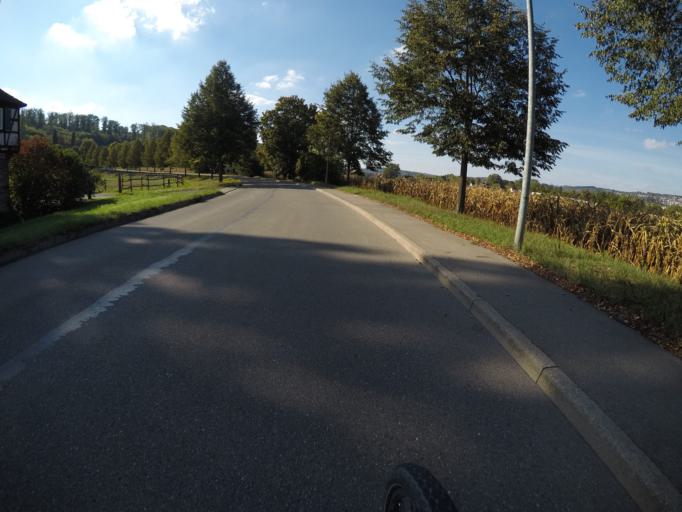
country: DE
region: Baden-Wuerttemberg
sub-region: Regierungsbezirk Stuttgart
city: Denkendorf
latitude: 48.7188
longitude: 9.3381
